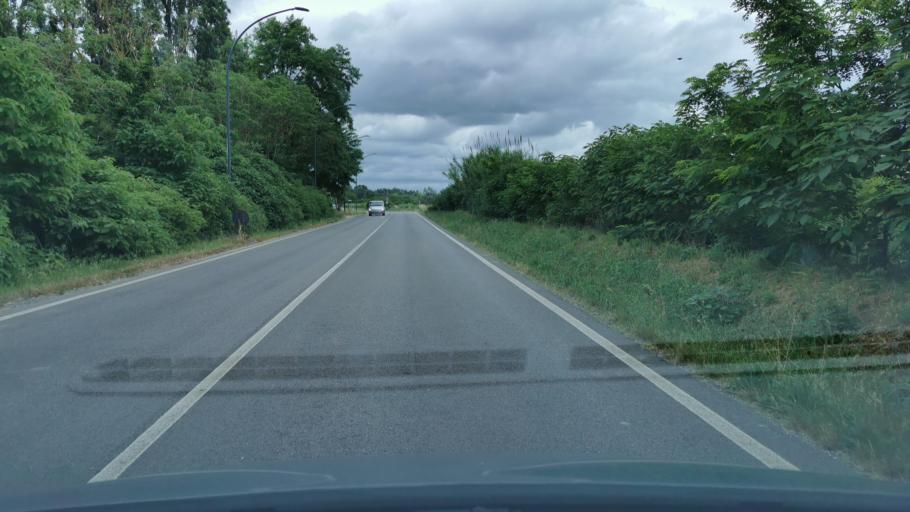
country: IT
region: Emilia-Romagna
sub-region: Provincia di Ravenna
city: Madonna Dell'Albero
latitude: 44.3883
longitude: 12.1965
